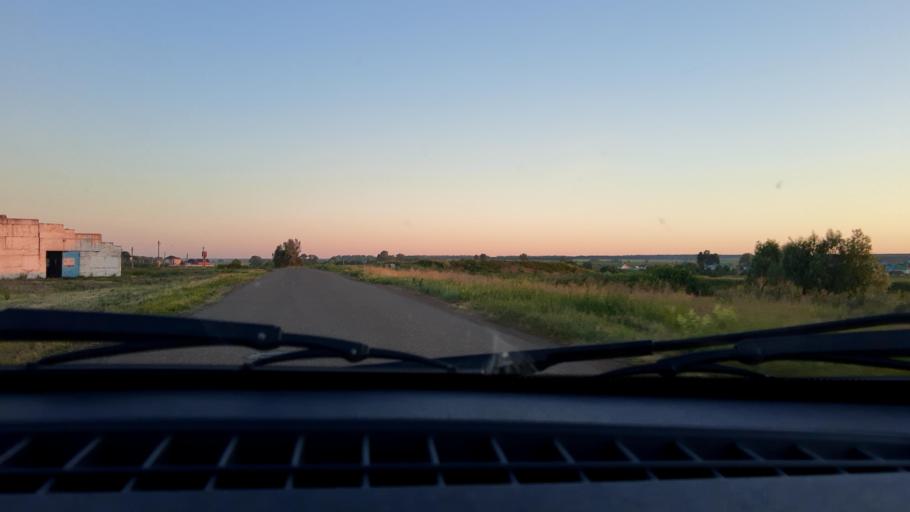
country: RU
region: Bashkortostan
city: Asanovo
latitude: 54.8990
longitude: 55.6277
